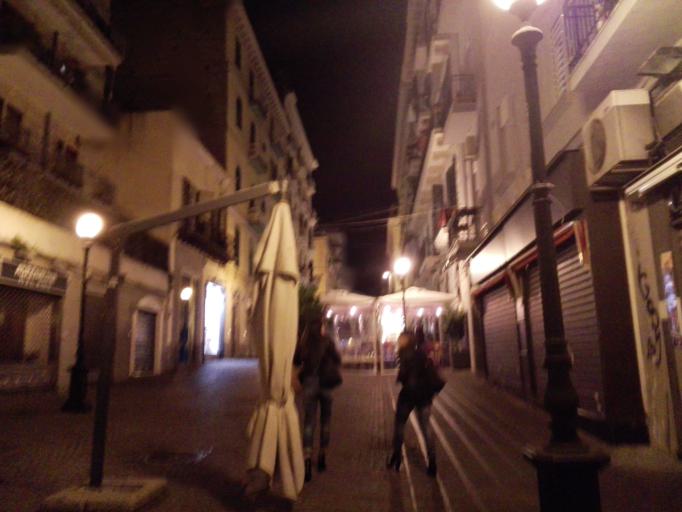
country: IT
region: Campania
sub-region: Provincia di Napoli
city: Napoli
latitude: 40.8444
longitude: 14.2292
